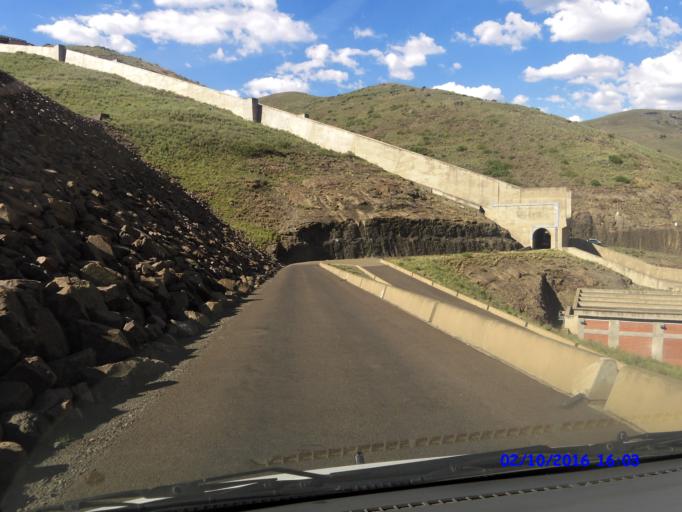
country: LS
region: Maseru
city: Nako
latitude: -29.4589
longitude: 28.0984
